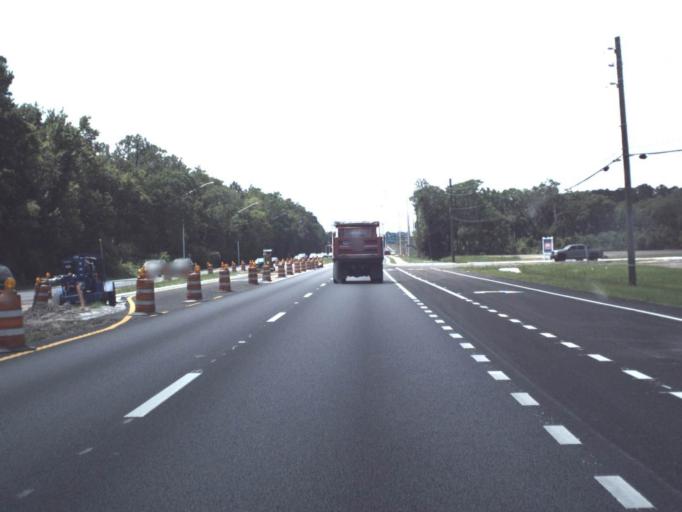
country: US
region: Florida
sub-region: Saint Johns County
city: Palm Valley
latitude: 30.1293
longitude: -81.5038
